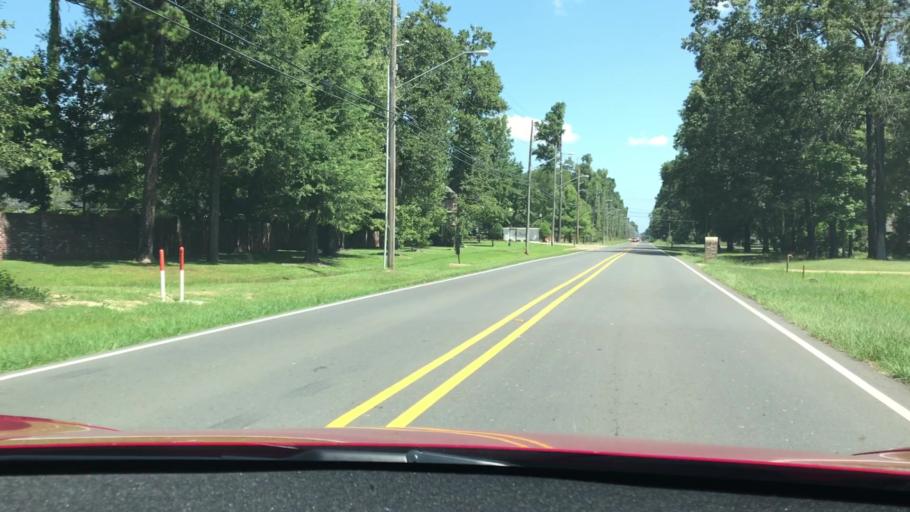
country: US
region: Louisiana
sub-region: De Soto Parish
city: Stonewall
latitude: 32.3450
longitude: -93.7138
